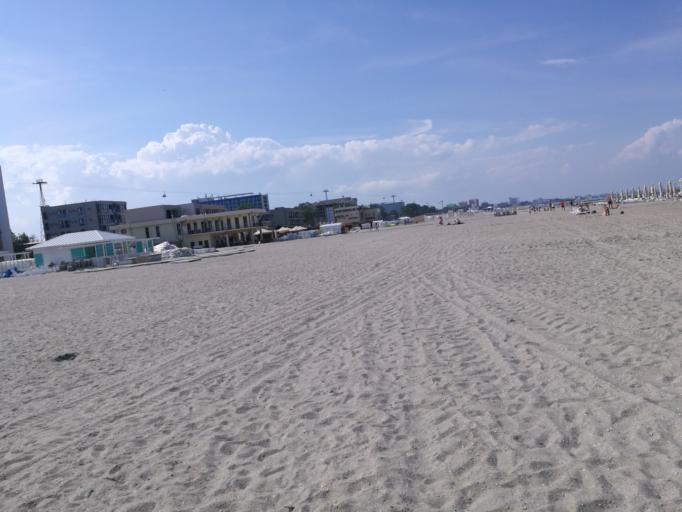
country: RO
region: Constanta
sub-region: Municipiul Constanta
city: Palazu Mare
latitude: 44.2248
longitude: 28.6326
